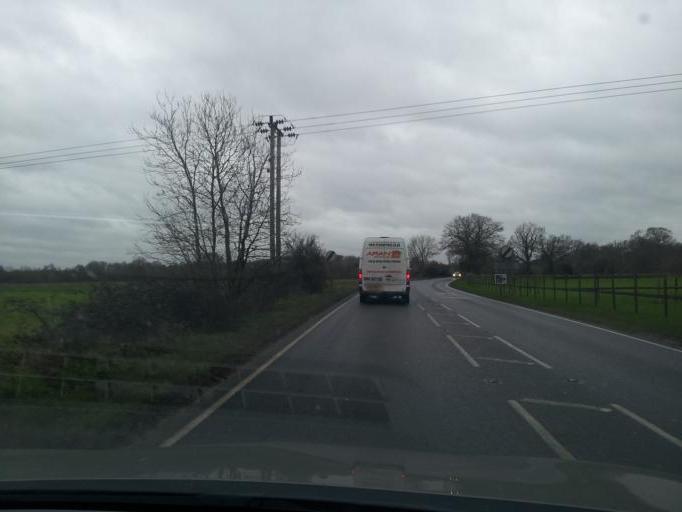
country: GB
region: England
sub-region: Suffolk
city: Ixworth
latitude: 52.3212
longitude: 0.8730
